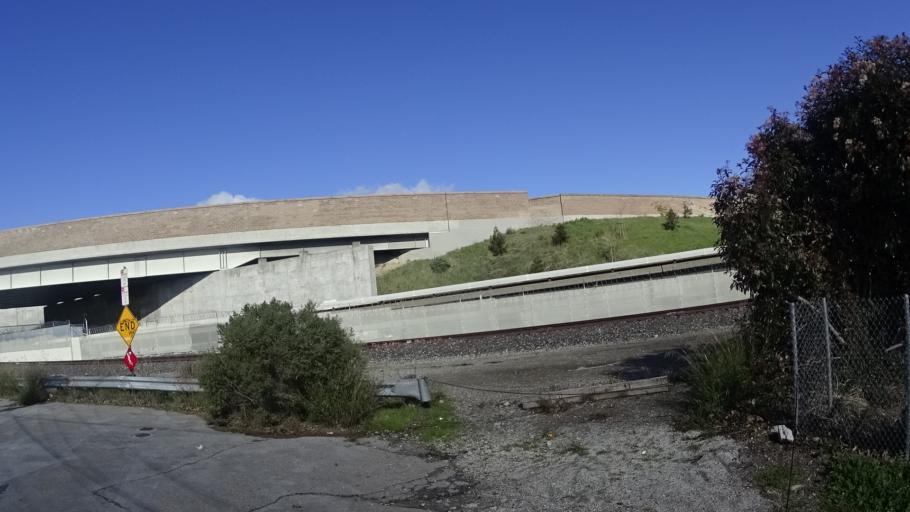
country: US
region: California
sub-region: Alameda County
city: Ashland
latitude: 37.6880
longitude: -122.1142
